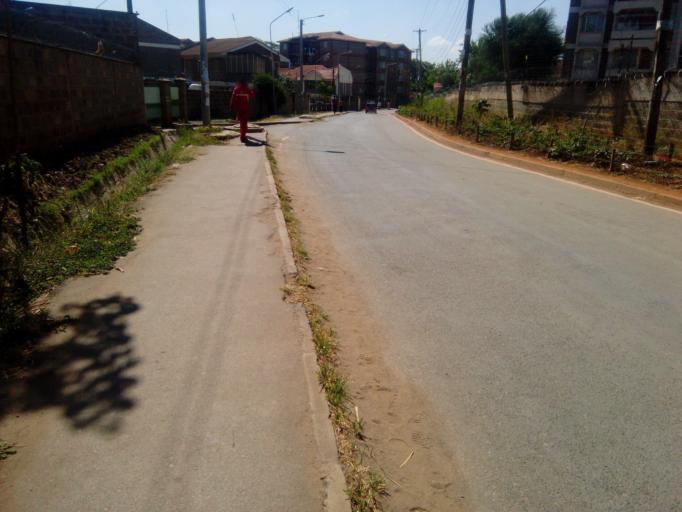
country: KE
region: Nairobi Area
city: Nairobi
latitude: -1.3052
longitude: 36.7752
